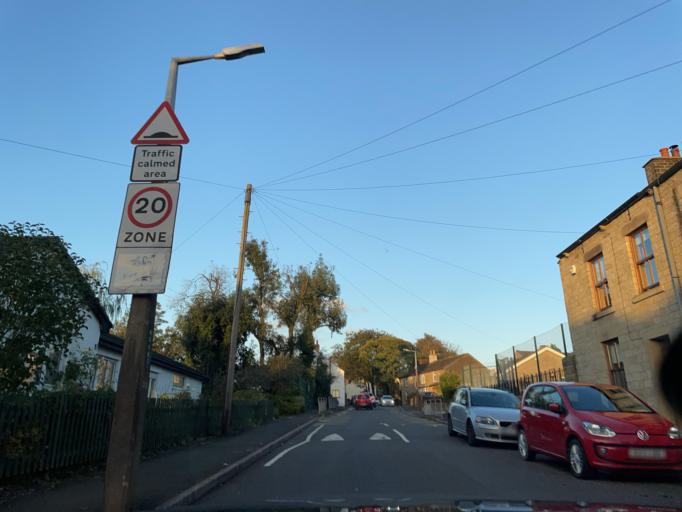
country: GB
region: England
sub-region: Borough of Tameside
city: Longdendale
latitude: 53.4601
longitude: -1.9725
